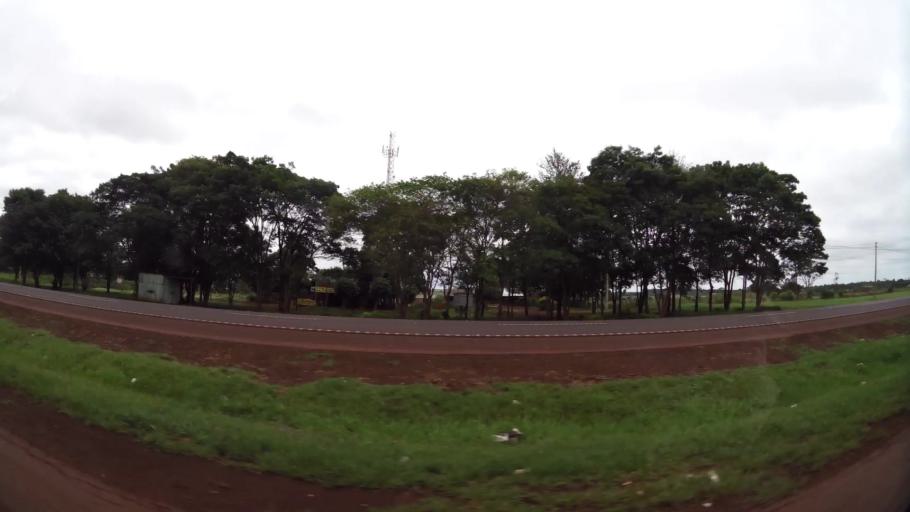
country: PY
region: Alto Parana
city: Colonia Yguazu
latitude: -25.4871
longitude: -54.8496
